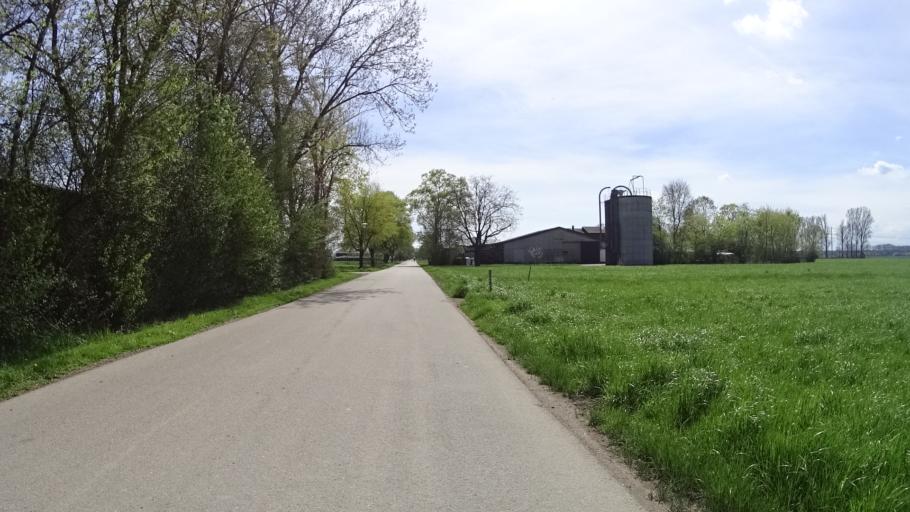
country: DE
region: Baden-Wuerttemberg
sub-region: Karlsruhe Region
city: Hemsbach
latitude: 49.6036
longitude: 8.6168
